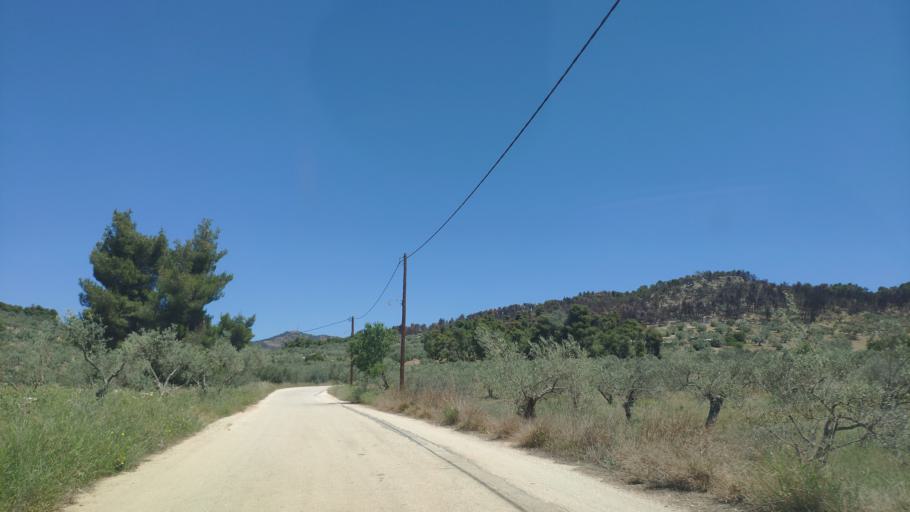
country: GR
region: Peloponnese
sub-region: Nomos Korinthias
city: Athikia
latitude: 37.8266
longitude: 22.9283
